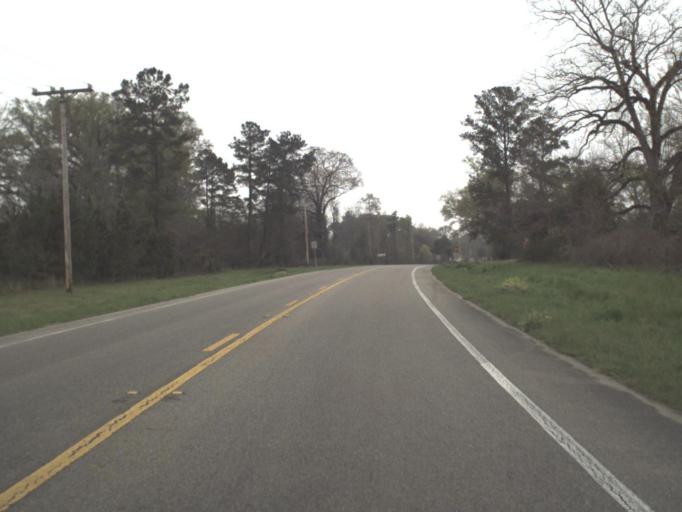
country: US
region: Florida
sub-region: Gadsden County
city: Gretna
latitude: 30.5888
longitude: -84.6717
